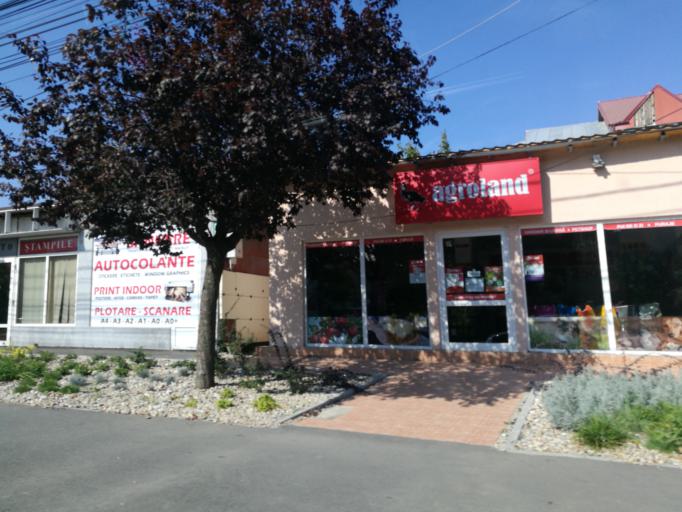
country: RO
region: Ilfov
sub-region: Comuna Otopeni
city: Otopeni
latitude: 44.5511
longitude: 26.0766
